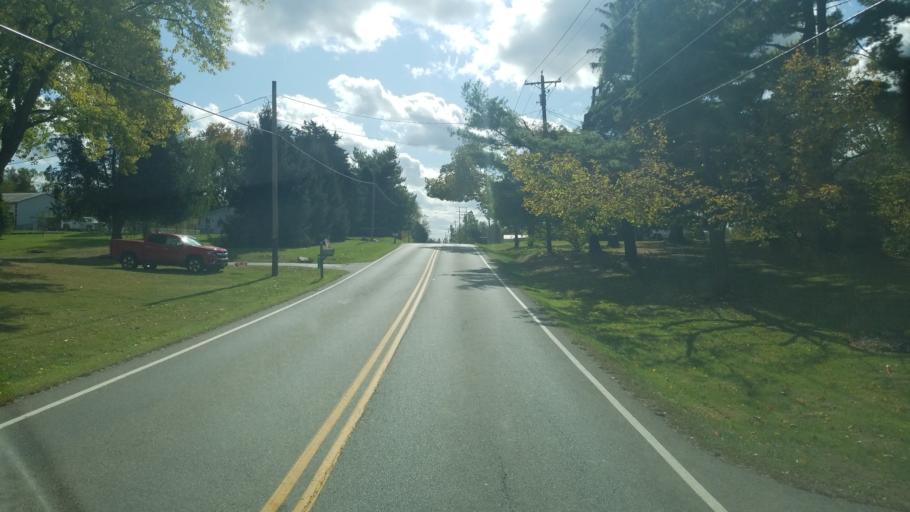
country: US
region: Ohio
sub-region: Warren County
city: South Lebanon
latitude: 39.3929
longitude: -84.1705
